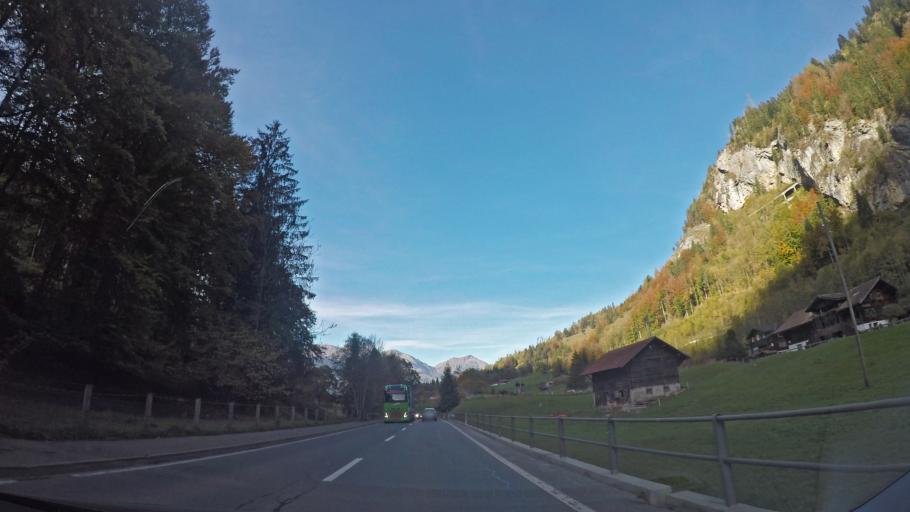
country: CH
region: Bern
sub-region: Frutigen-Niedersimmental District
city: Kandersteg
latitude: 46.5409
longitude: 7.6670
